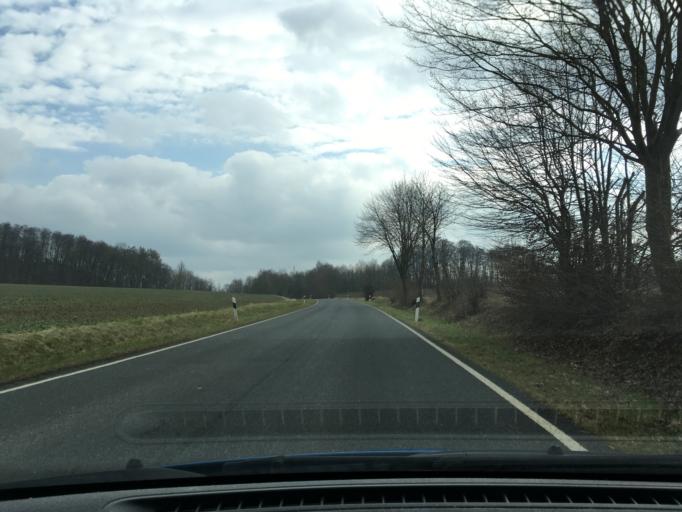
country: DE
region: Lower Saxony
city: Adelebsen
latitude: 51.5599
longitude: 9.7395
